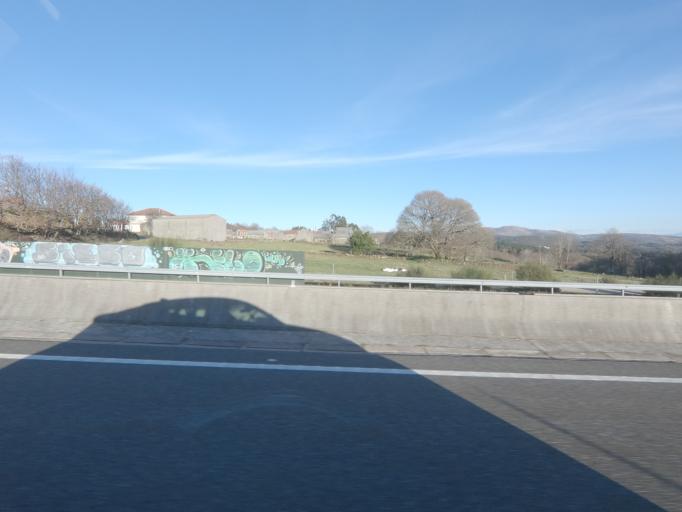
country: ES
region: Galicia
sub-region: Provincia de Pontevedra
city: Dozon
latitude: 42.5435
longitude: -8.0204
